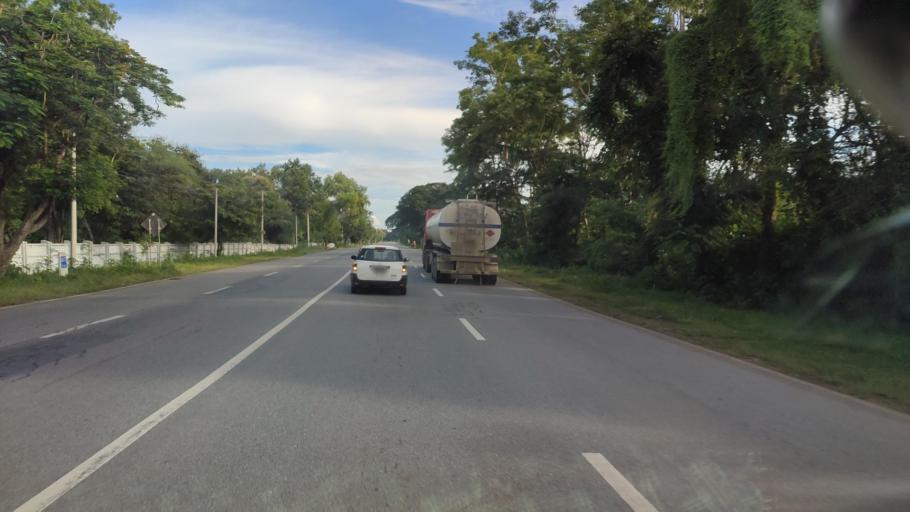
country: MM
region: Mandalay
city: Yamethin
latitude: 20.1580
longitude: 96.1912
